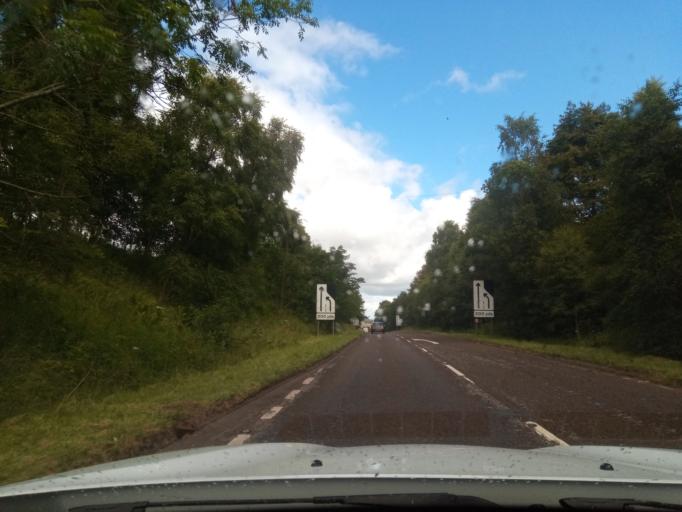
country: GB
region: Scotland
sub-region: Stirling
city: Dunblane
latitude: 56.1772
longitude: -3.9663
